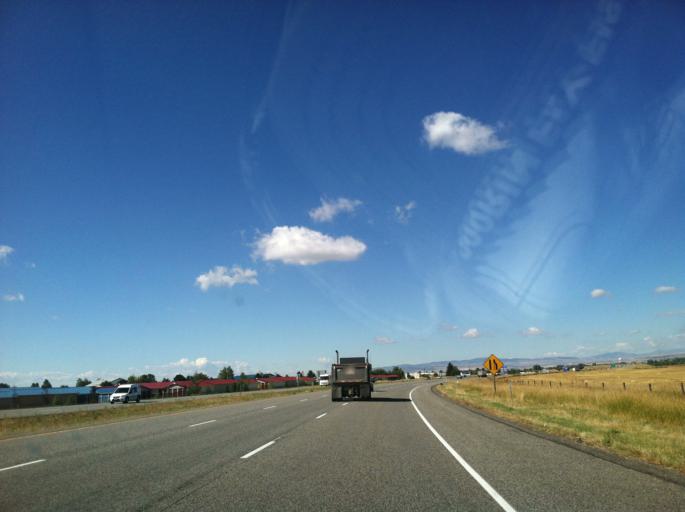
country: US
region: Montana
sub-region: Gallatin County
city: Bozeman
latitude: 45.7039
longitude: -111.0595
